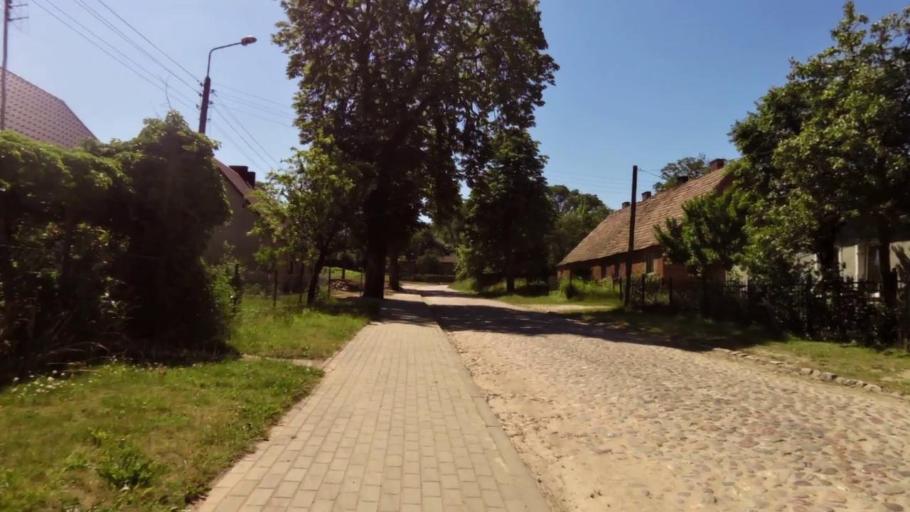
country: PL
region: West Pomeranian Voivodeship
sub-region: Powiat swidwinski
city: Rabino
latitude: 53.8841
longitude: 16.0116
